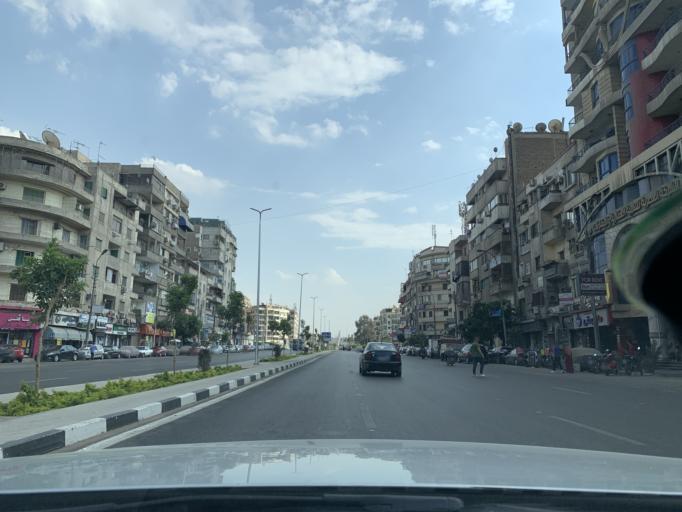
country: EG
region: Muhafazat al Qahirah
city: Cairo
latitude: 30.1026
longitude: 31.3434
